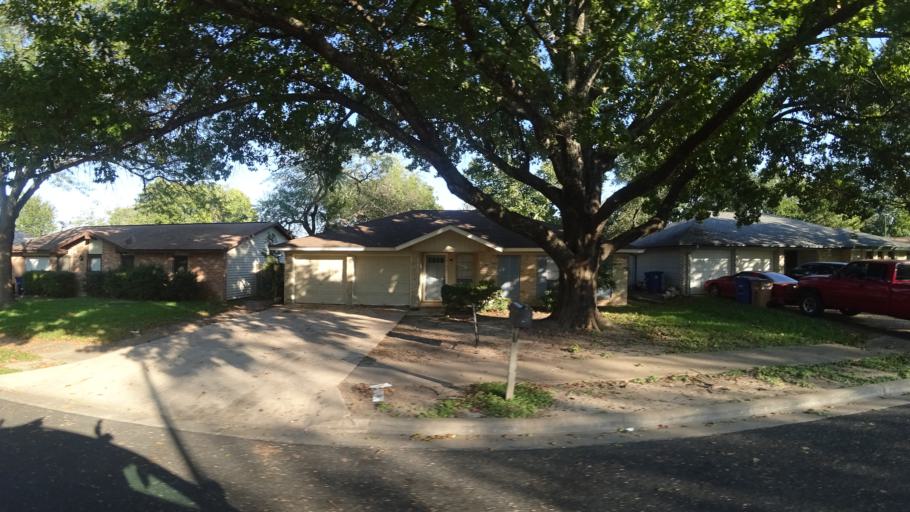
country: US
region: Texas
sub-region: Travis County
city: Wells Branch
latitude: 30.3628
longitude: -97.6778
